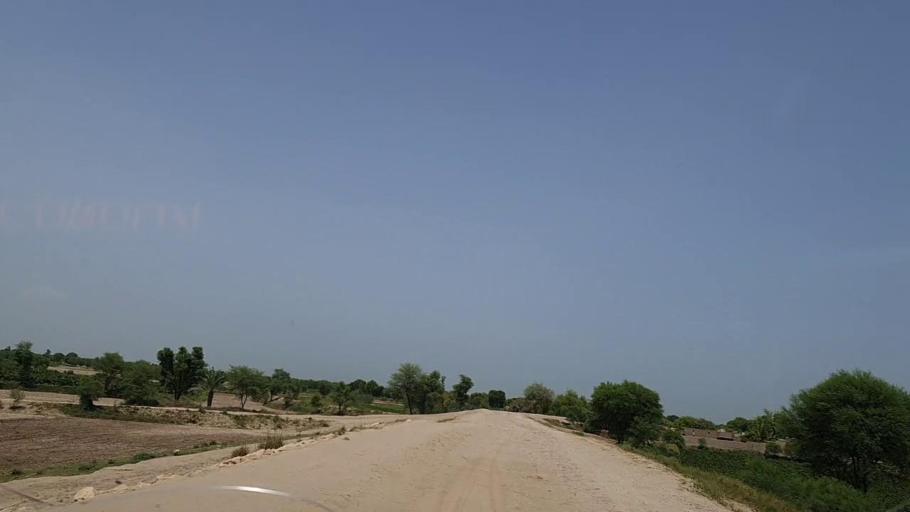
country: PK
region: Sindh
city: Tharu Shah
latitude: 27.0206
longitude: 68.1092
